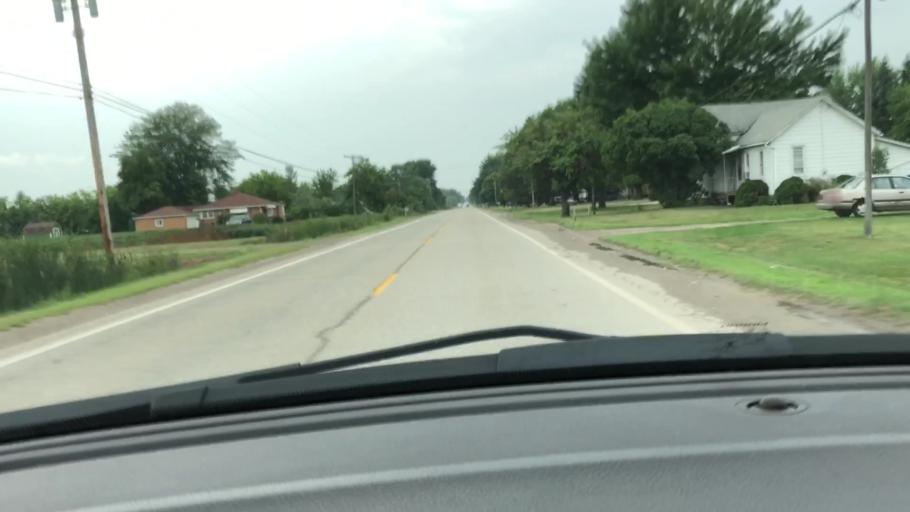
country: US
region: Michigan
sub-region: Bay County
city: Auburn
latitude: 43.6041
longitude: -84.1168
